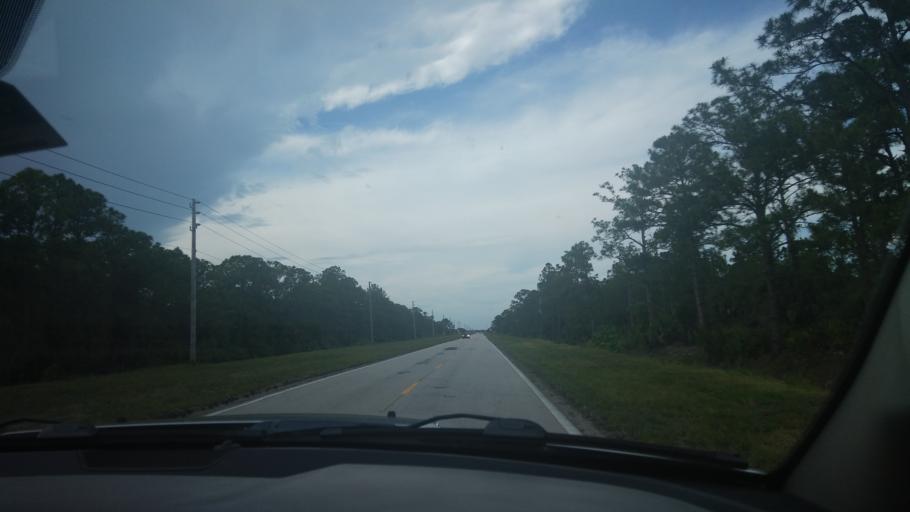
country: US
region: Florida
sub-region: Brevard County
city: Grant-Valkaria
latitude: 27.8831
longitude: -80.6225
